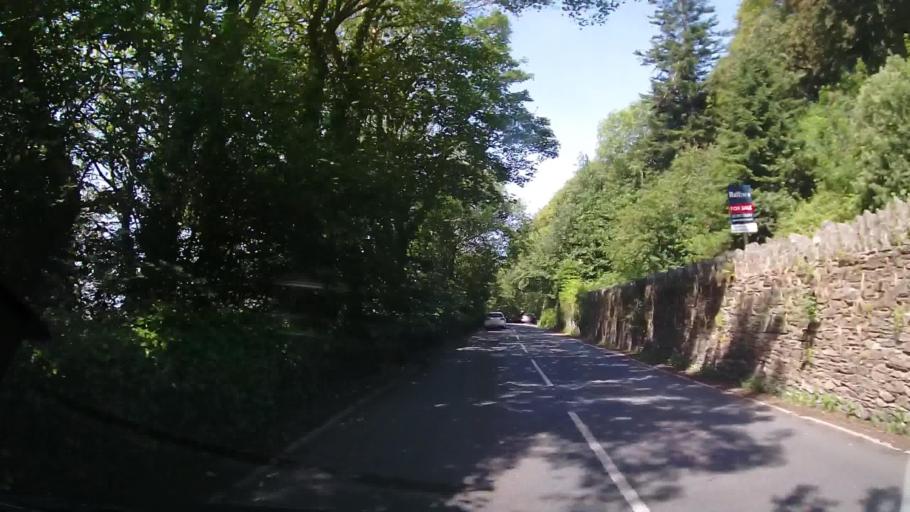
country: GB
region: Wales
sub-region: Gwynedd
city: Tywyn
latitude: 52.5476
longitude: -4.0144
